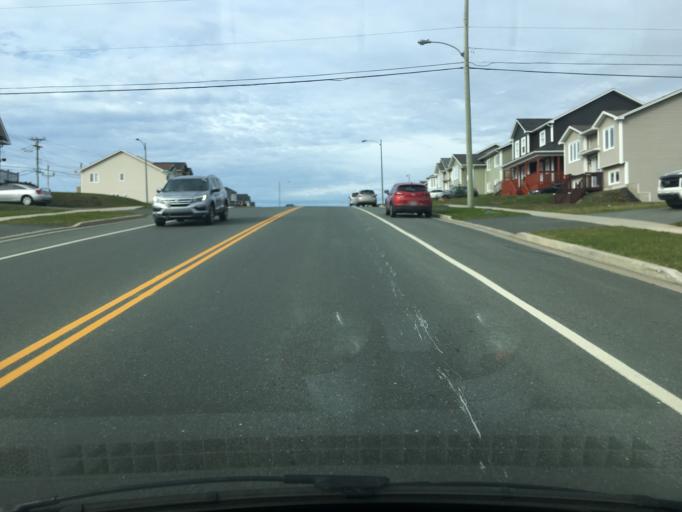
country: CA
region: Newfoundland and Labrador
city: Mount Pearl
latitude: 47.5497
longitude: -52.7885
